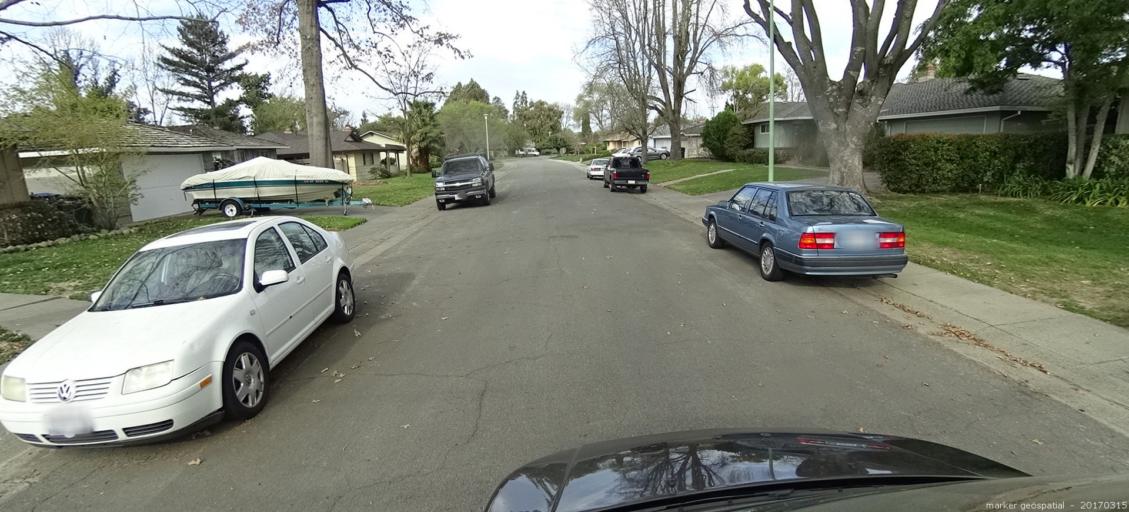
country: US
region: California
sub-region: Sacramento County
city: Parkway
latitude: 38.5088
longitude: -121.5112
